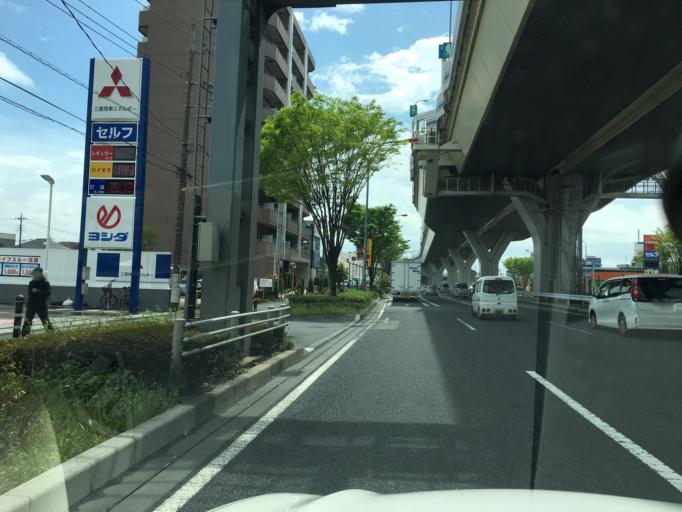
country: JP
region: Saitama
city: Asaka
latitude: 35.8299
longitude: 139.6357
